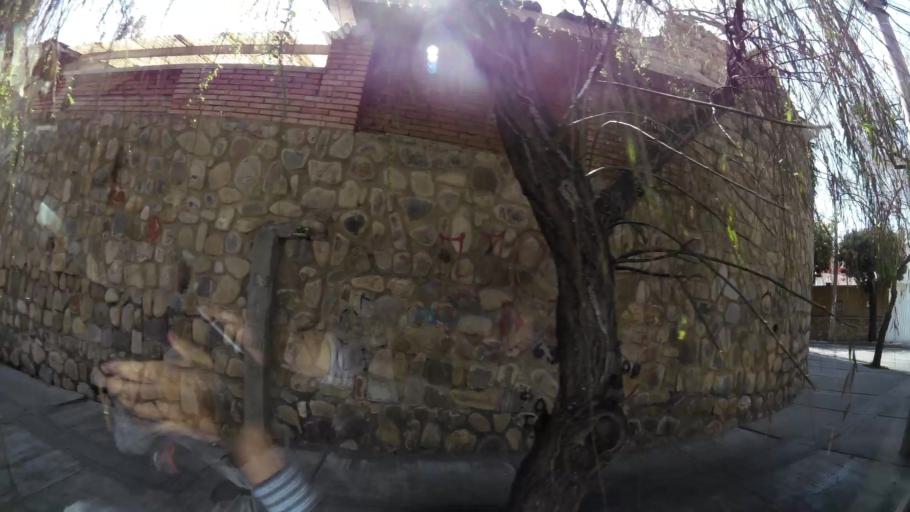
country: BO
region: La Paz
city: La Paz
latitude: -16.5440
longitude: -68.0878
